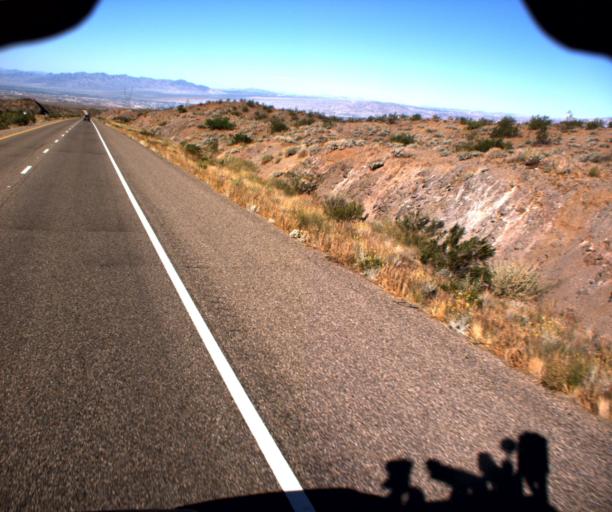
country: US
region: Nevada
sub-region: Clark County
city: Laughlin
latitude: 35.1912
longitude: -114.4446
